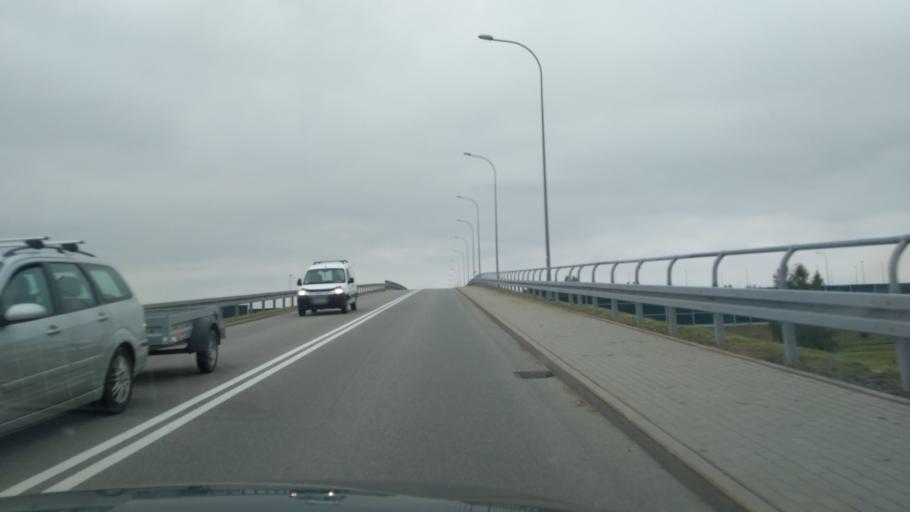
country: PL
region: Subcarpathian Voivodeship
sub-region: Powiat ropczycko-sedziszowski
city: Sedziszow Malopolski
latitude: 50.1094
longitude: 21.6714
